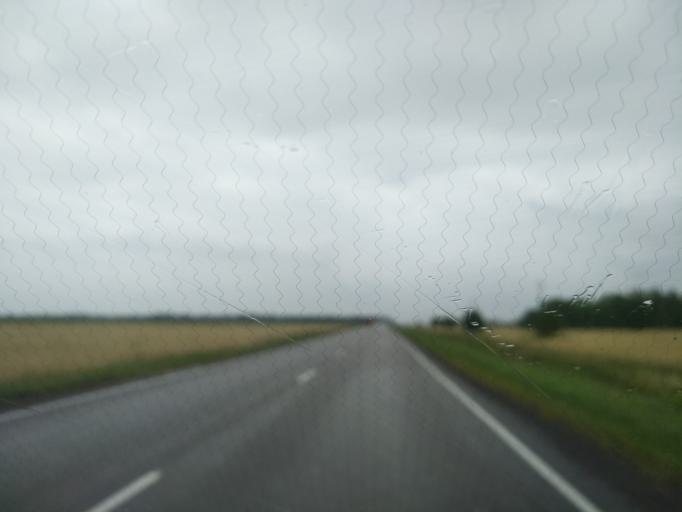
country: RU
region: Voronezj
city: Orlovo
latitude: 51.6769
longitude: 39.7755
